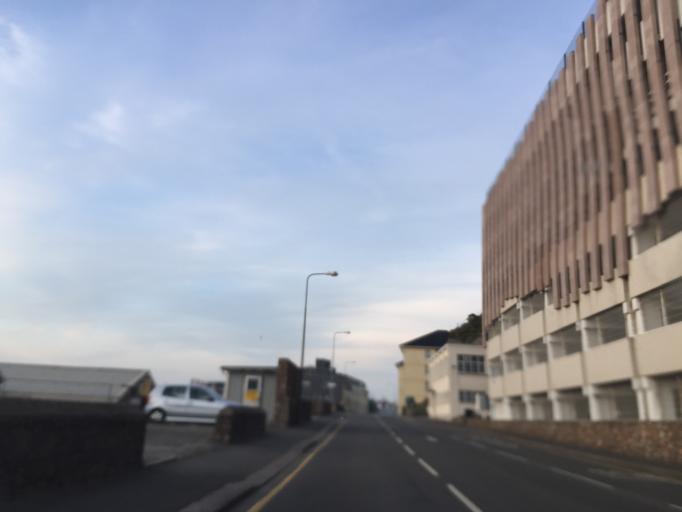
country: JE
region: St Helier
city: Saint Helier
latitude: 49.1804
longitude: -2.1081
